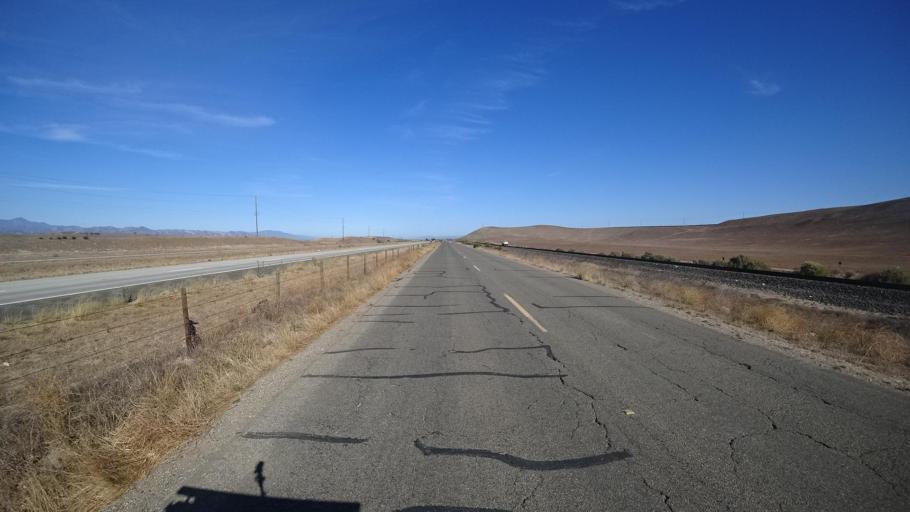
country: US
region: California
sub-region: Monterey County
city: King City
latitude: 36.1513
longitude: -121.0430
